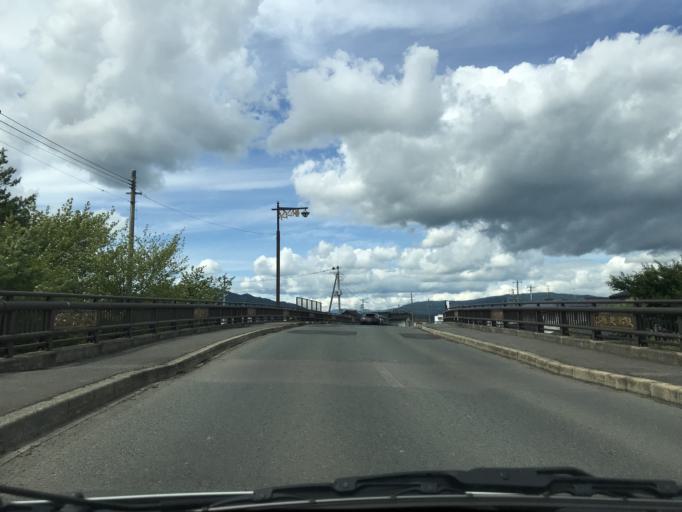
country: JP
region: Iwate
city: Tono
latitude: 39.3311
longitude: 141.5367
